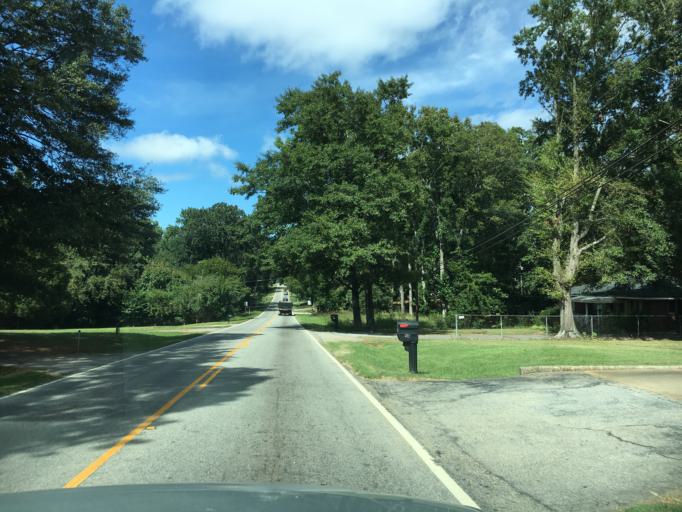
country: US
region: South Carolina
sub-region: Spartanburg County
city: Lyman
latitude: 34.9601
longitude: -82.1249
